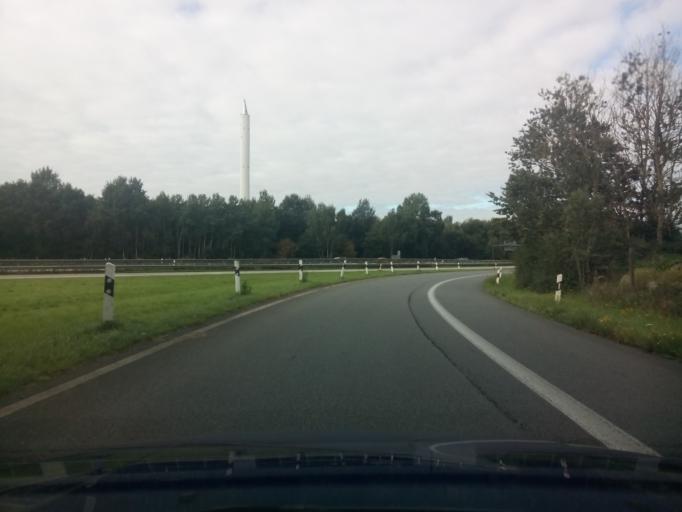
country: DE
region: Lower Saxony
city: Lilienthal
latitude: 53.1120
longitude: 8.8655
